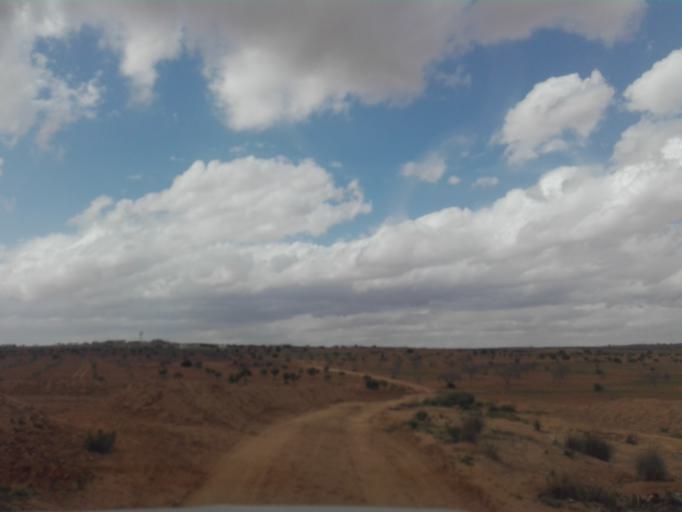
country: TN
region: Safaqis
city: Sfax
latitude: 34.6986
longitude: 10.4428
